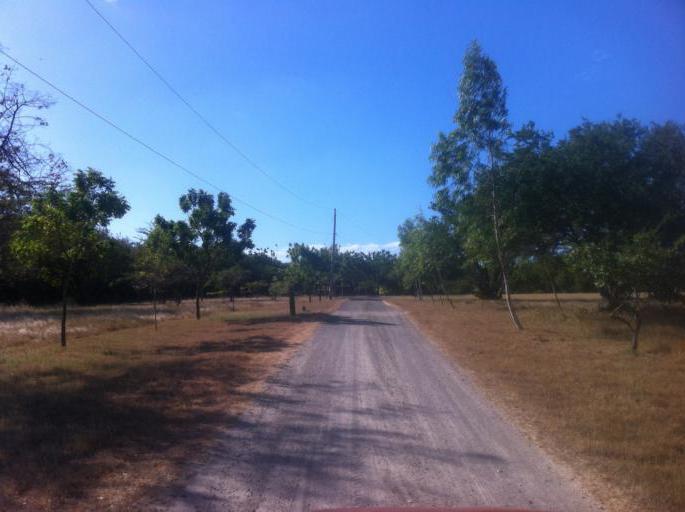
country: NI
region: Managua
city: Carlos Fonseca Amador
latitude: 11.9017
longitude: -86.6084
